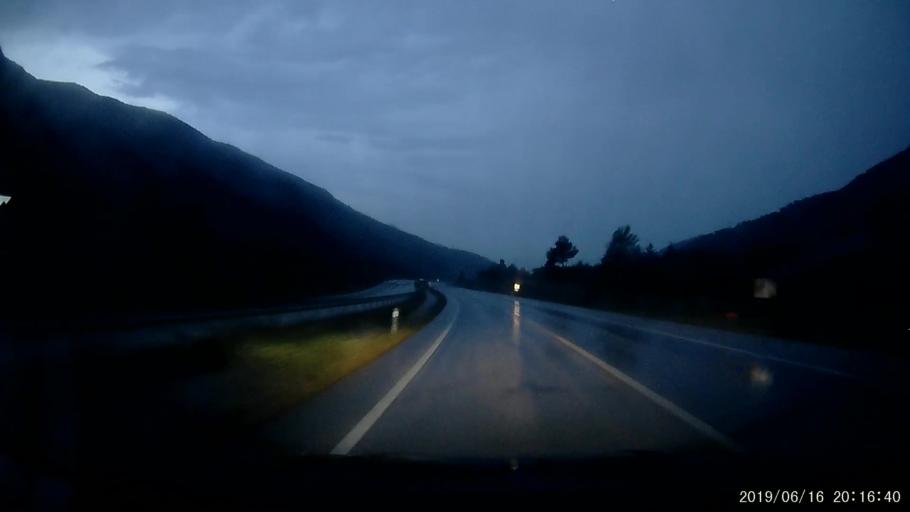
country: TR
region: Tokat
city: Resadiye
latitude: 40.3601
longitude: 37.4368
